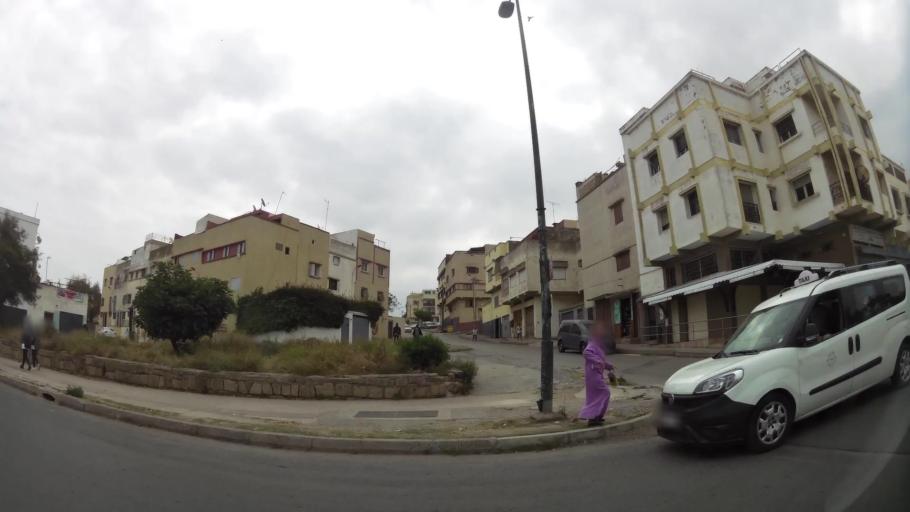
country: MA
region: Rabat-Sale-Zemmour-Zaer
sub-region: Rabat
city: Rabat
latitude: 33.9919
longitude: -6.8782
